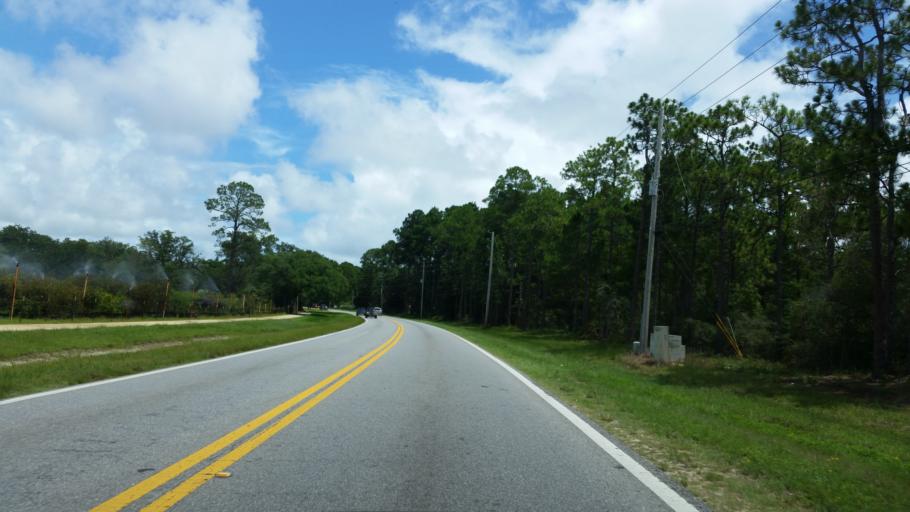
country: US
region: Florida
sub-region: Santa Rosa County
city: Holley
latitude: 30.4352
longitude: -86.9157
